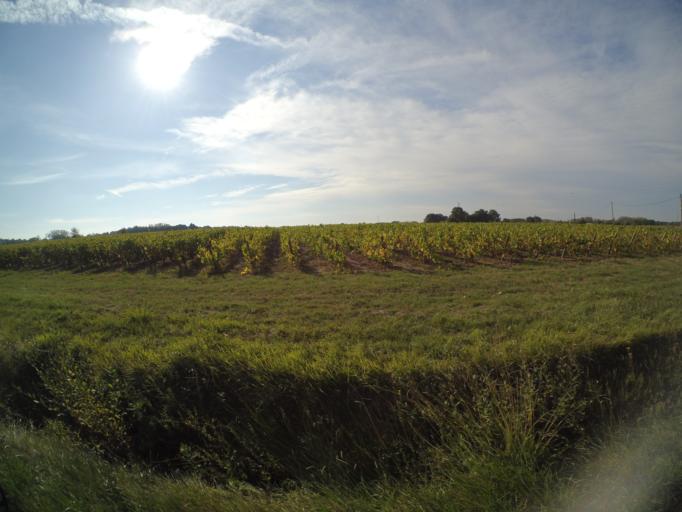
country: FR
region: Pays de la Loire
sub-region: Departement de la Loire-Atlantique
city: Mouzillon
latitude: 47.1274
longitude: -1.2648
